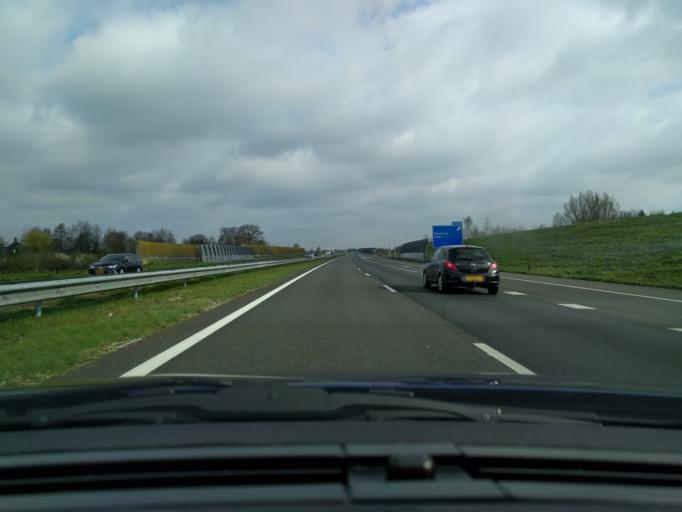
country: NL
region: North Brabant
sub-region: Gemeente Uden
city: Uden
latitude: 51.6644
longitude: 5.5999
